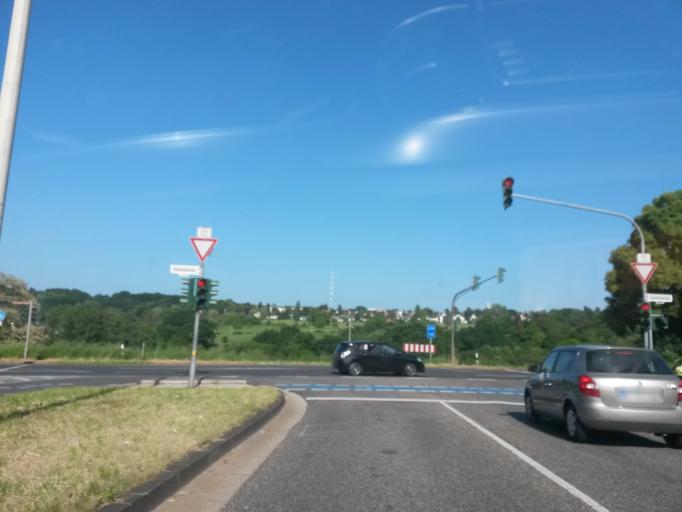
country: DE
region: North Rhine-Westphalia
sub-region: Regierungsbezirk Koln
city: Bonn
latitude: 50.7053
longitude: 7.0689
